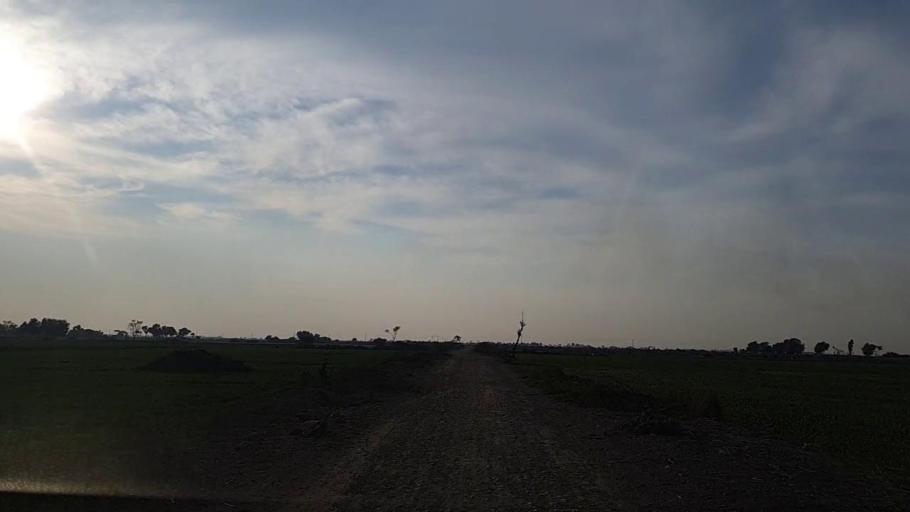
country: PK
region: Sindh
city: Bandhi
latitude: 26.5649
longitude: 68.2524
